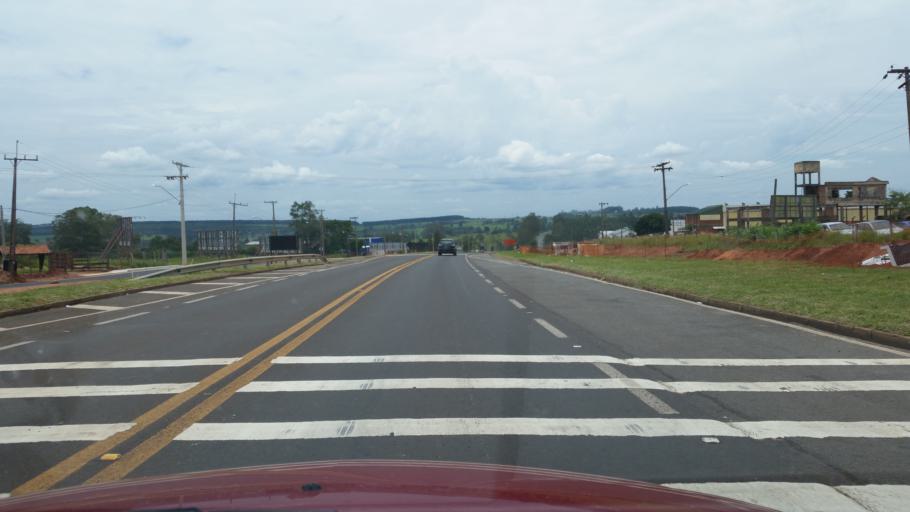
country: BR
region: Sao Paulo
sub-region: Avare
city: Avare
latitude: -23.0761
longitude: -48.9270
